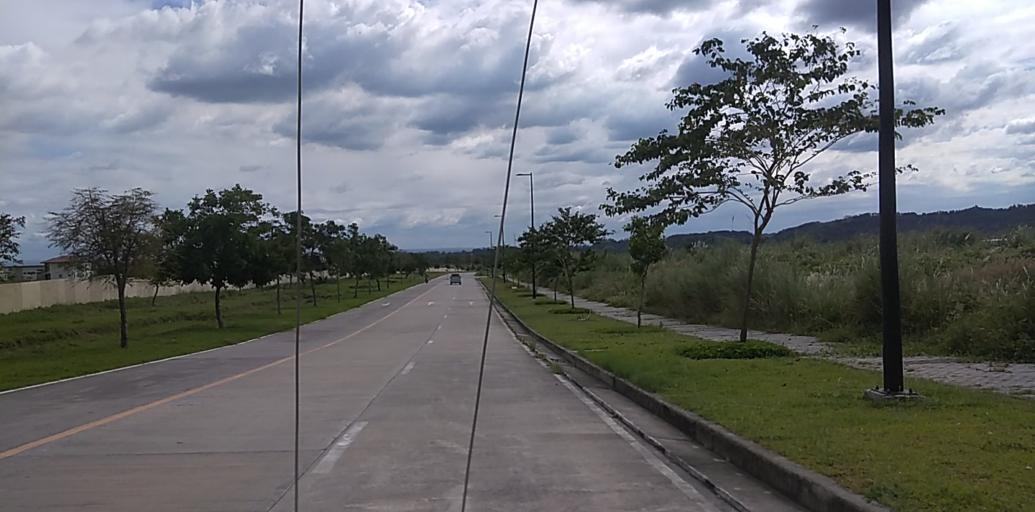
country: PH
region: Central Luzon
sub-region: Province of Pampanga
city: Dolores
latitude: 15.1154
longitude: 120.5124
